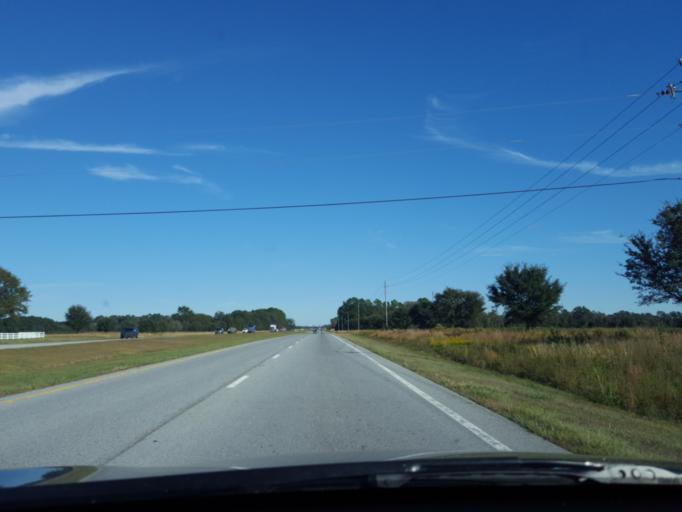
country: US
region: North Carolina
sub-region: Pitt County
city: Greenville
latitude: 35.6256
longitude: -77.2913
